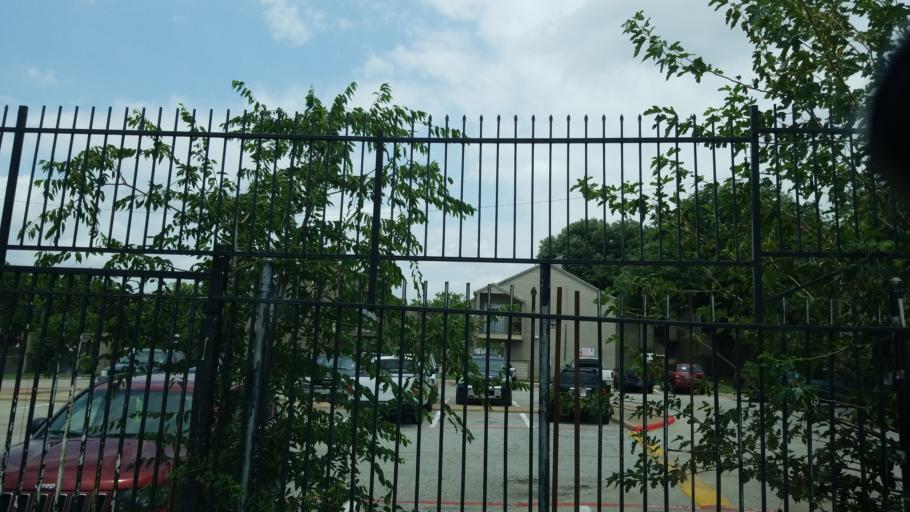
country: US
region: Texas
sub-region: Dallas County
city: Farmers Branch
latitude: 32.8725
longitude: -96.8660
